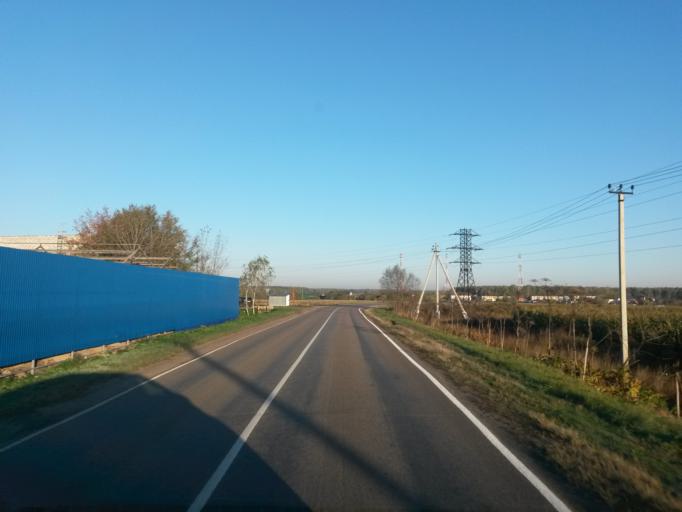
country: RU
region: Moskovskaya
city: Belyye Stolby
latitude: 55.2620
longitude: 37.7656
